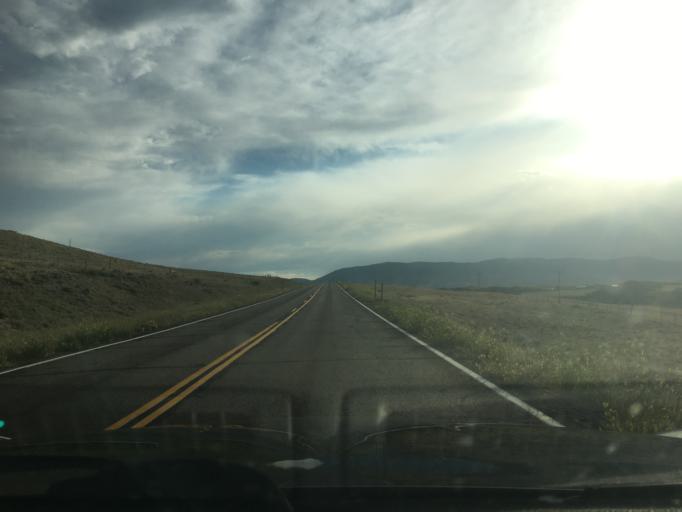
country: US
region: Wyoming
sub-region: Albany County
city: Laramie
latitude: 41.2850
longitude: -106.0517
